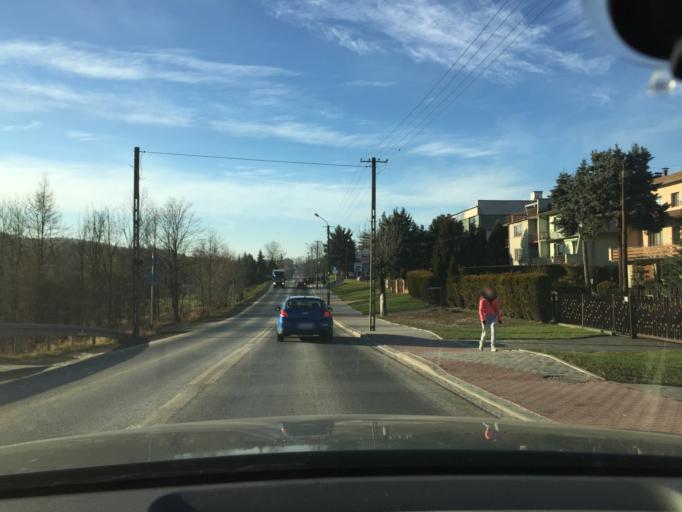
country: PL
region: Lesser Poland Voivodeship
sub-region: Powiat wadowicki
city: Brody
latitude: 49.8663
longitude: 19.6887
